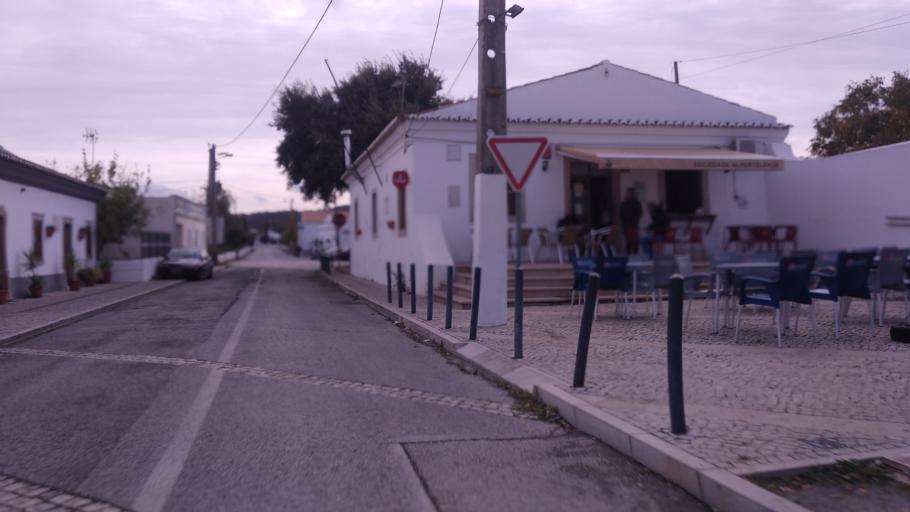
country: PT
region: Faro
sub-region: Sao Bras de Alportel
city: Sao Bras de Alportel
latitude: 37.1755
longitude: -7.9092
